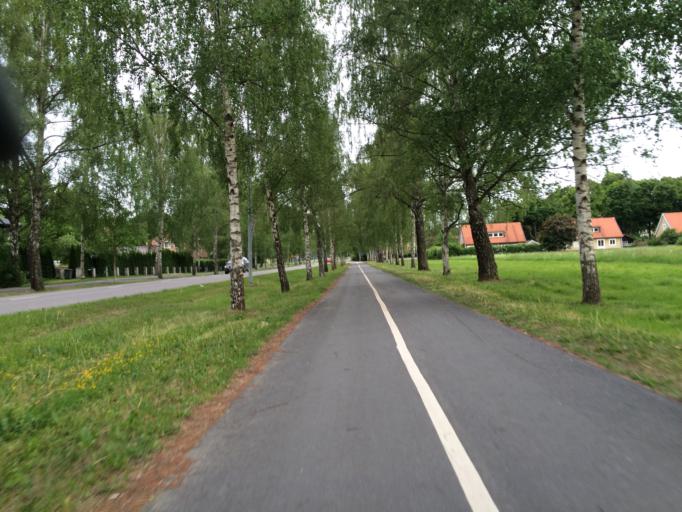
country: SE
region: Stockholm
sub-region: Danderyds Kommun
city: Djursholm
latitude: 59.3984
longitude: 18.0832
